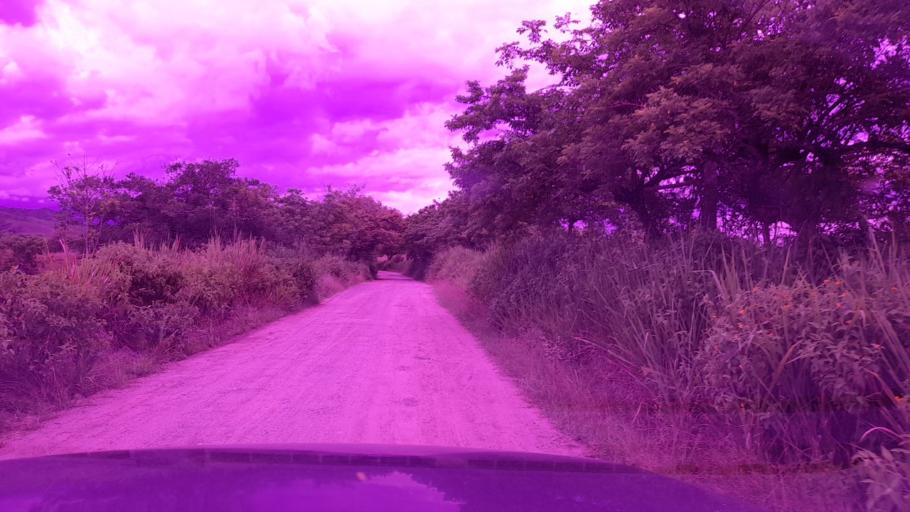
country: CO
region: Valle del Cauca
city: Andalucia
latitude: 4.1823
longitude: -76.1374
